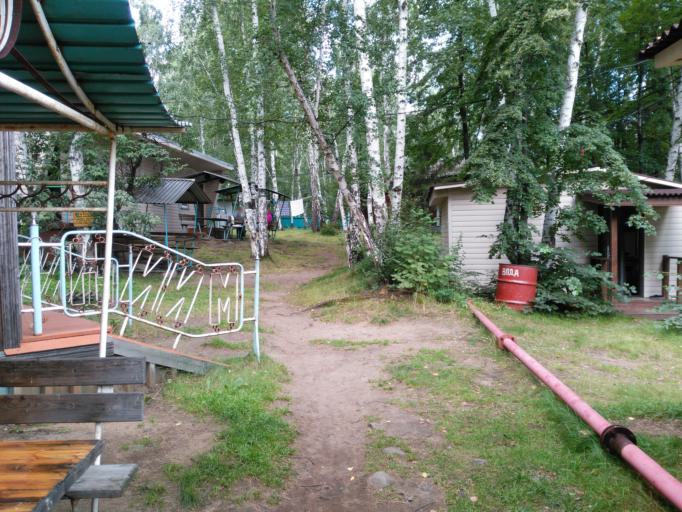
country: RU
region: Chelyabinsk
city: Tayginka
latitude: 55.4792
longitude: 60.4976
